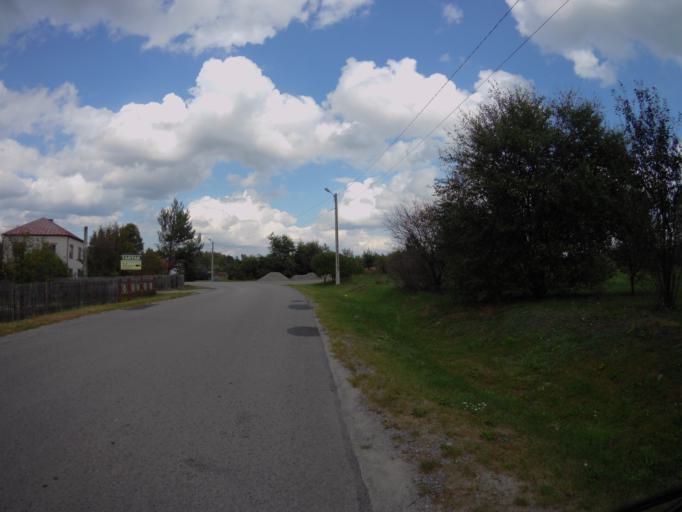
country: PL
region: Subcarpathian Voivodeship
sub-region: Powiat lezajski
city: Brzoza Krolewska
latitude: 50.2414
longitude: 22.3277
